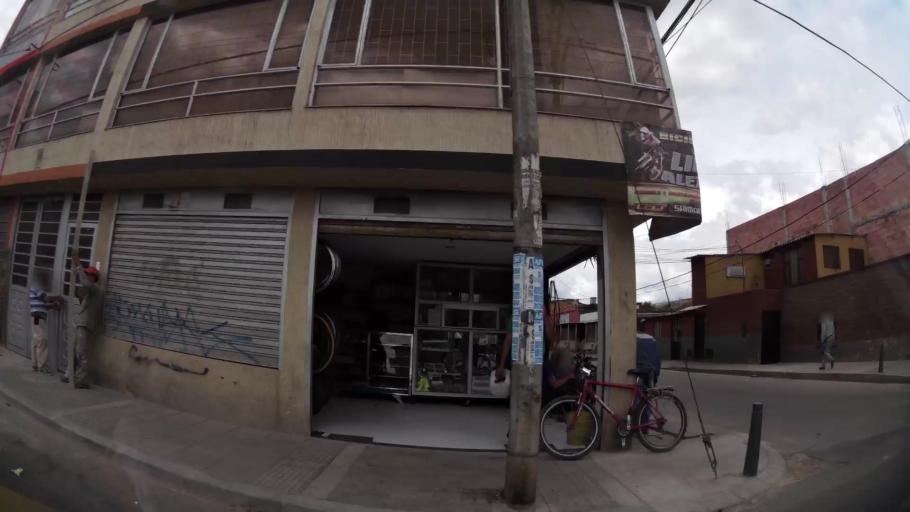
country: CO
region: Cundinamarca
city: Funza
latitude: 4.7161
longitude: -74.1426
